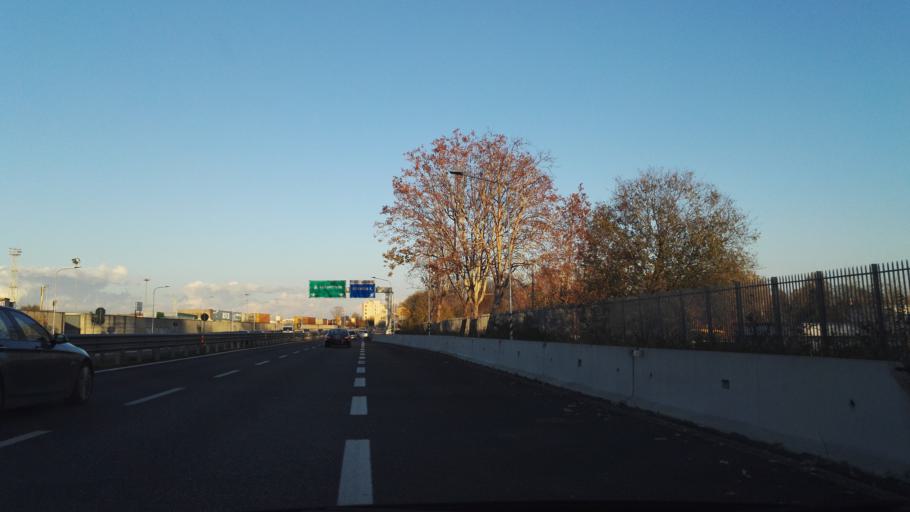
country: IT
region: Lombardy
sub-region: Citta metropolitana di Milano
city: Novegro-Tregarezzo-San Felice
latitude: 45.4757
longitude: 9.2904
